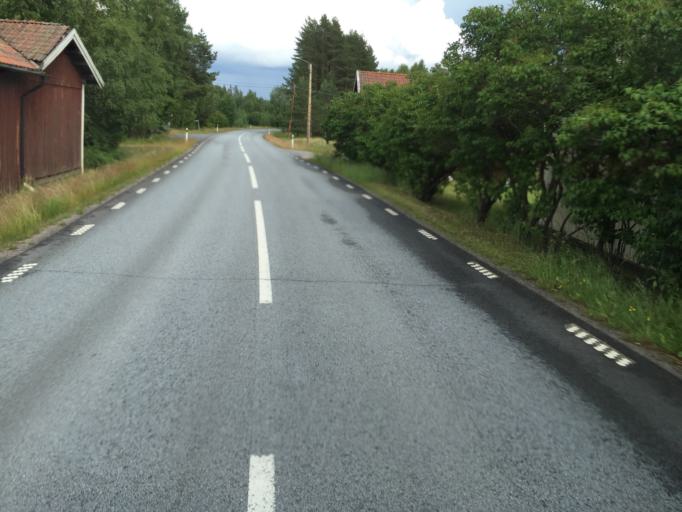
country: SE
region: Dalarna
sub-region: Vansbro Kommun
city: Vansbro
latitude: 60.5215
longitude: 14.2920
